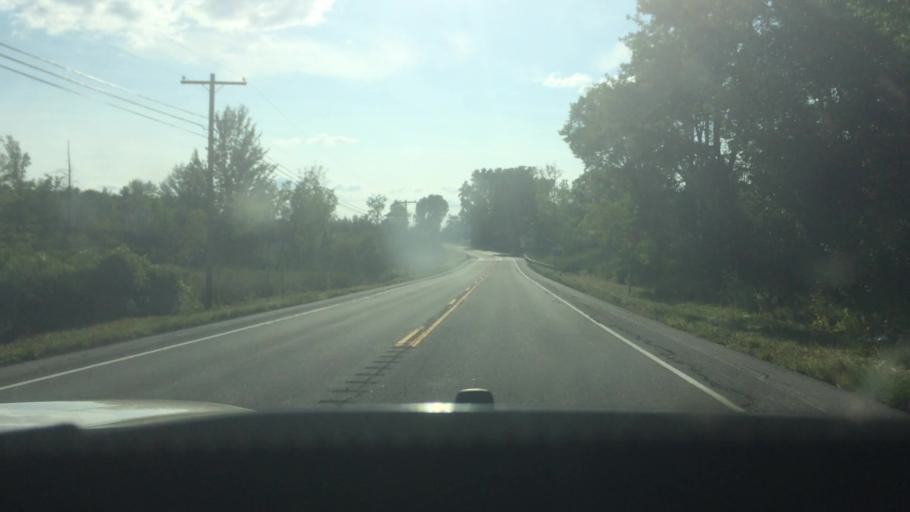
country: US
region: New York
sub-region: St. Lawrence County
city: Potsdam
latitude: 44.6854
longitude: -74.8017
